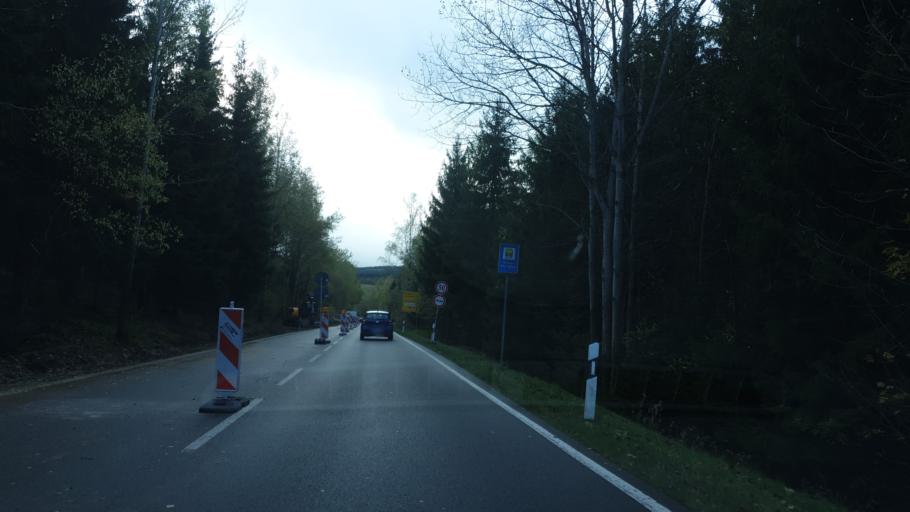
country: DE
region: Saxony
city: Eibenstock
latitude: 50.5094
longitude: 12.5951
